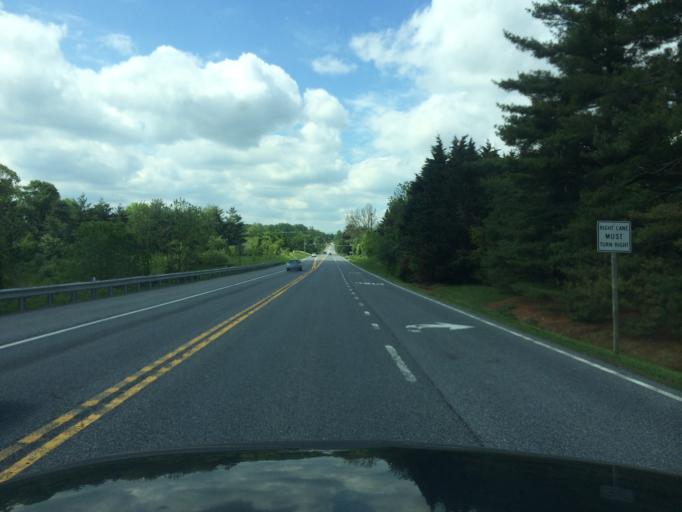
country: US
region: Maryland
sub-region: Carroll County
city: Westminster
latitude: 39.5585
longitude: -76.9816
